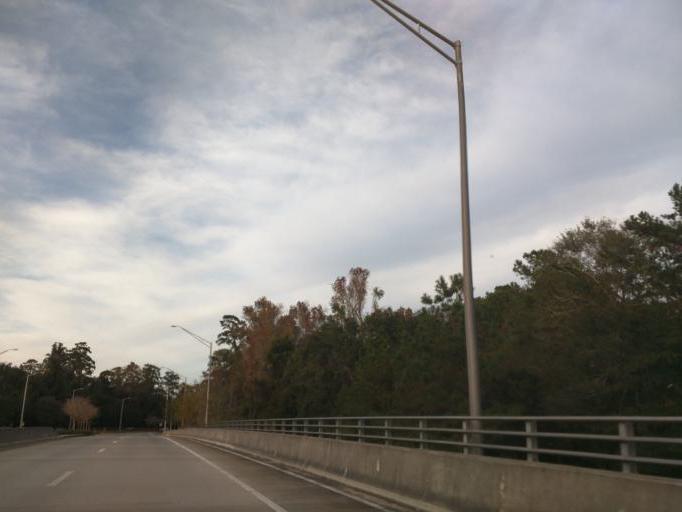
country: US
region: Florida
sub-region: Leon County
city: Tallahassee
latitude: 30.4483
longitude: -84.2507
